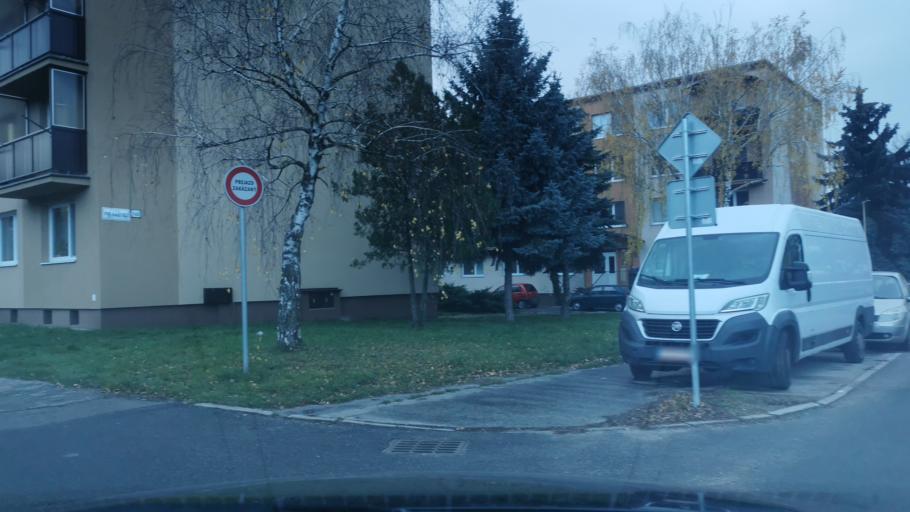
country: SK
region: Trnavsky
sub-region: Okres Skalica
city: Holic
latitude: 48.8059
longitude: 17.1612
